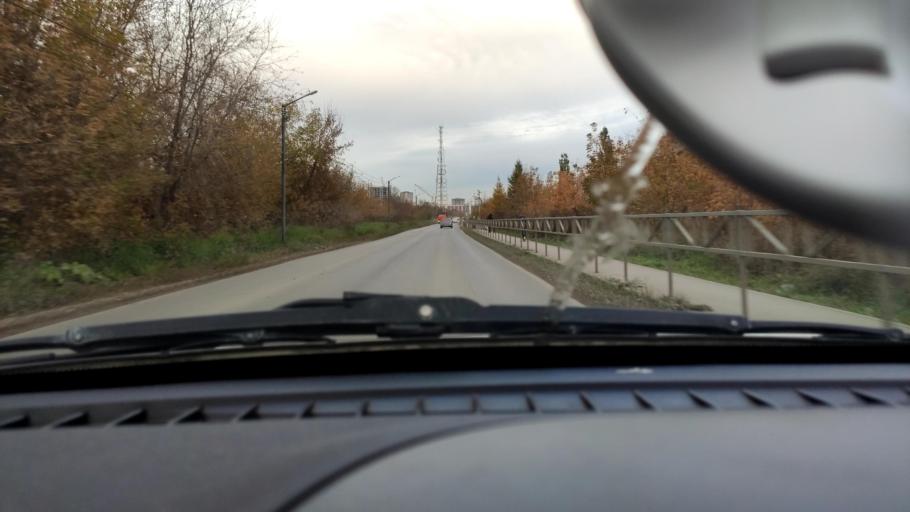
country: RU
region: Perm
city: Kondratovo
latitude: 57.9810
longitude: 56.1117
